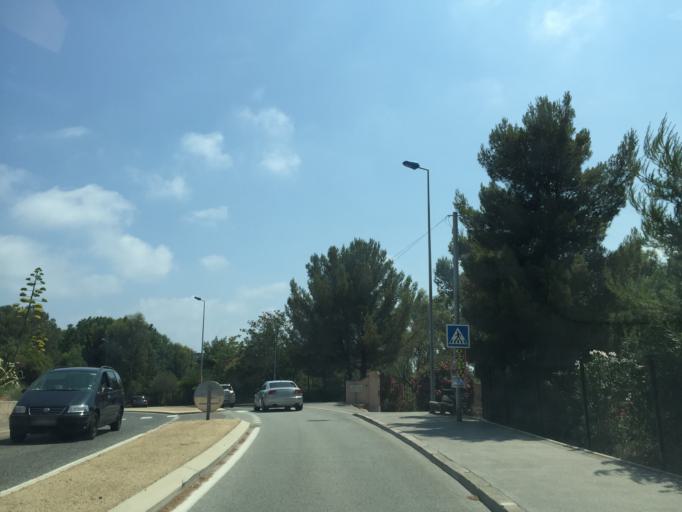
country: FR
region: Provence-Alpes-Cote d'Azur
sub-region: Departement du Var
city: Saint-Raphael
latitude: 43.4321
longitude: 6.8693
